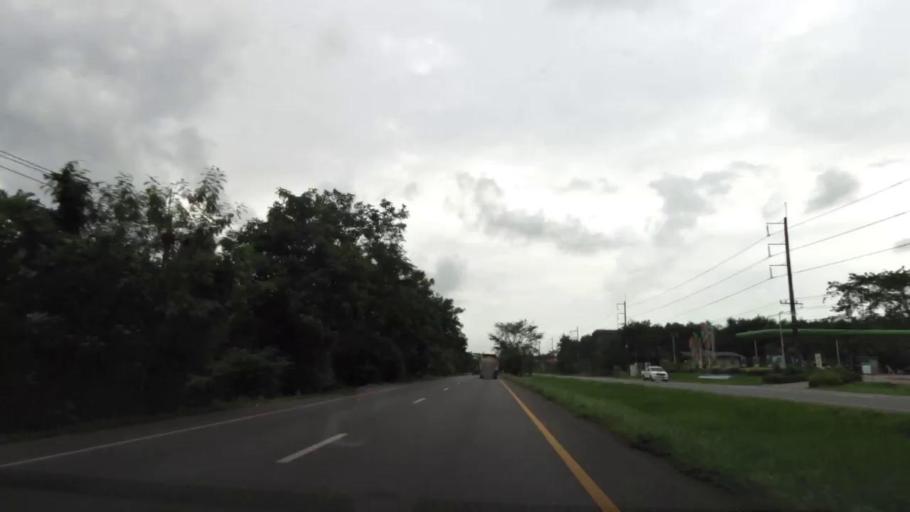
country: TH
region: Chanthaburi
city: Tha Mai
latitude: 12.7115
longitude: 101.9814
